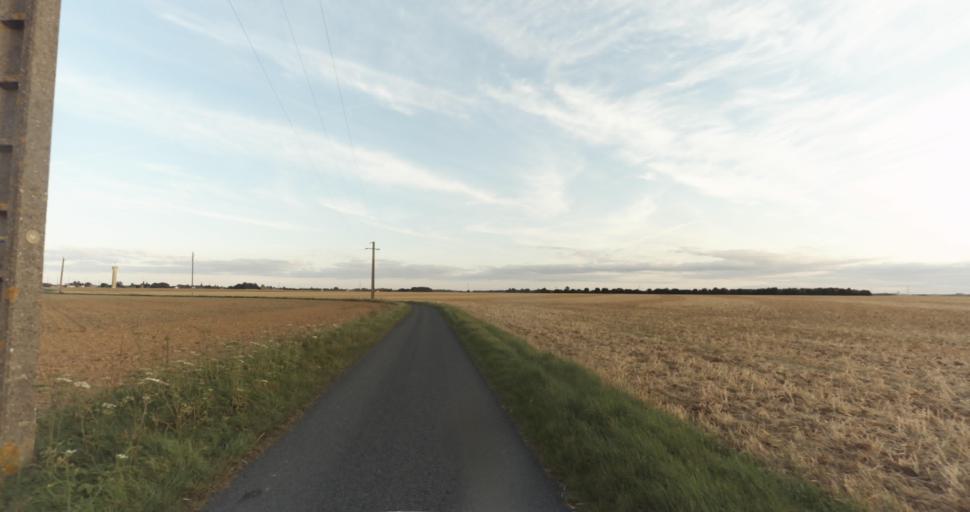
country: FR
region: Haute-Normandie
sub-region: Departement de l'Eure
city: La Madeleine-de-Nonancourt
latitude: 48.8779
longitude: 1.2291
